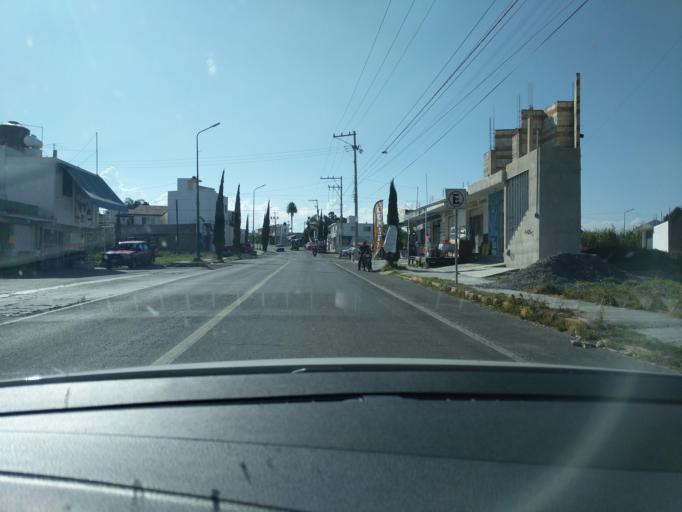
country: MX
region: Puebla
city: Tlazcalancingo
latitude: 19.0233
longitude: -98.3066
